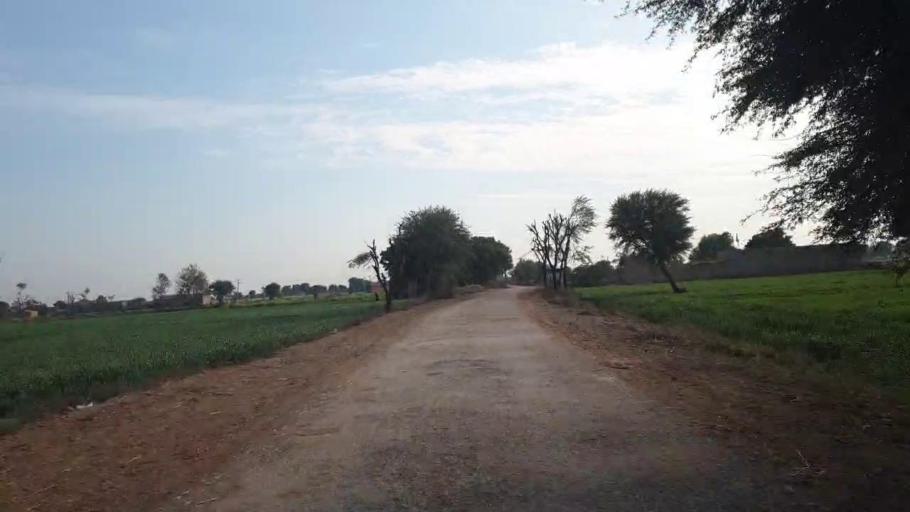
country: PK
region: Sindh
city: Shahpur Chakar
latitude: 26.0495
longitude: 68.5645
